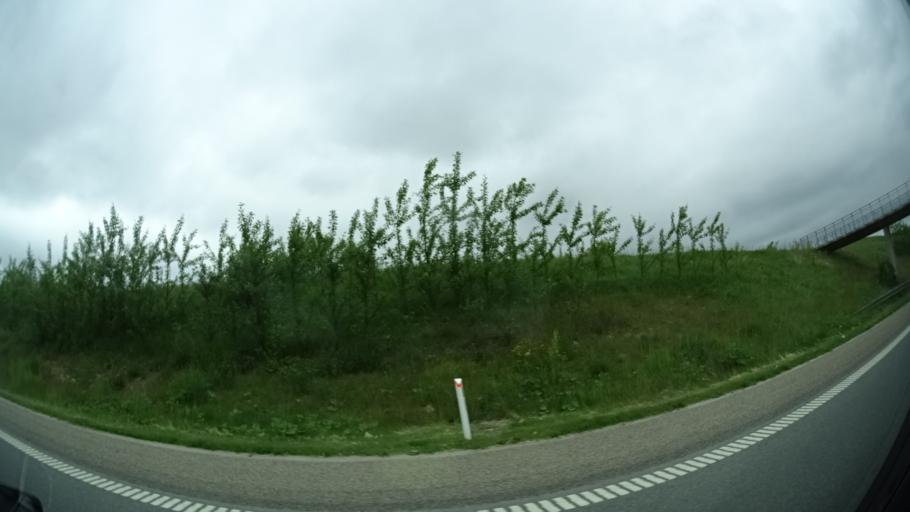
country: DK
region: Central Jutland
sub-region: Arhus Kommune
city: Hjortshoj
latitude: 56.2302
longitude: 10.2592
